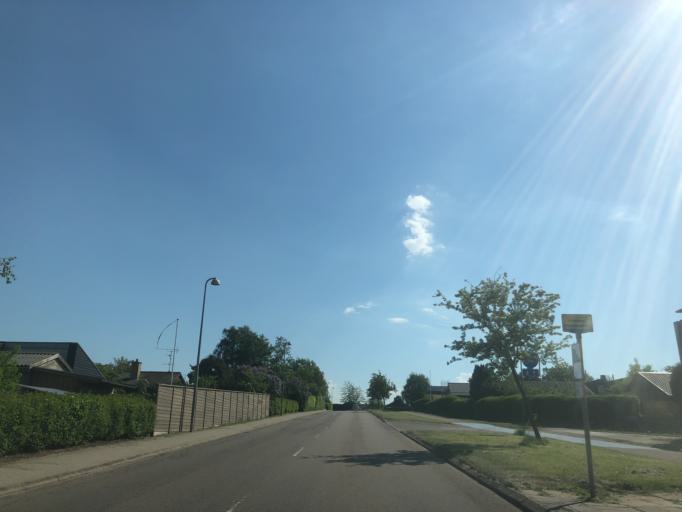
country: DK
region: Zealand
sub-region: Solrod Kommune
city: Havdrup
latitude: 55.5709
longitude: 12.0912
